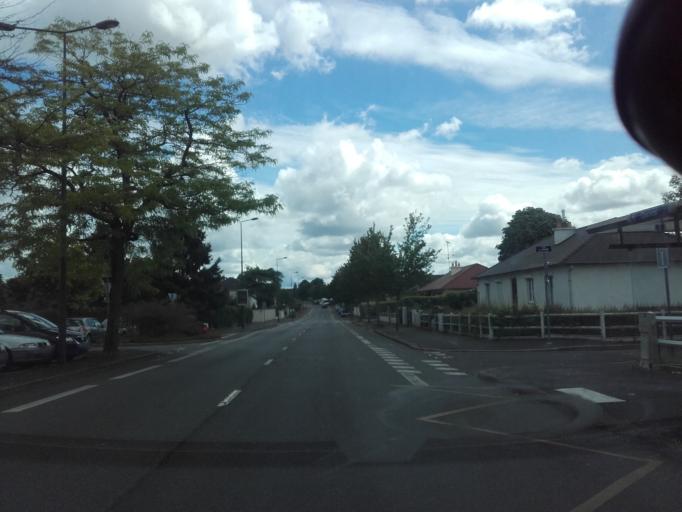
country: FR
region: Centre
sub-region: Departement d'Indre-et-Loire
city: Saint-Cyr-sur-Loire
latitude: 47.4261
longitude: 0.6834
